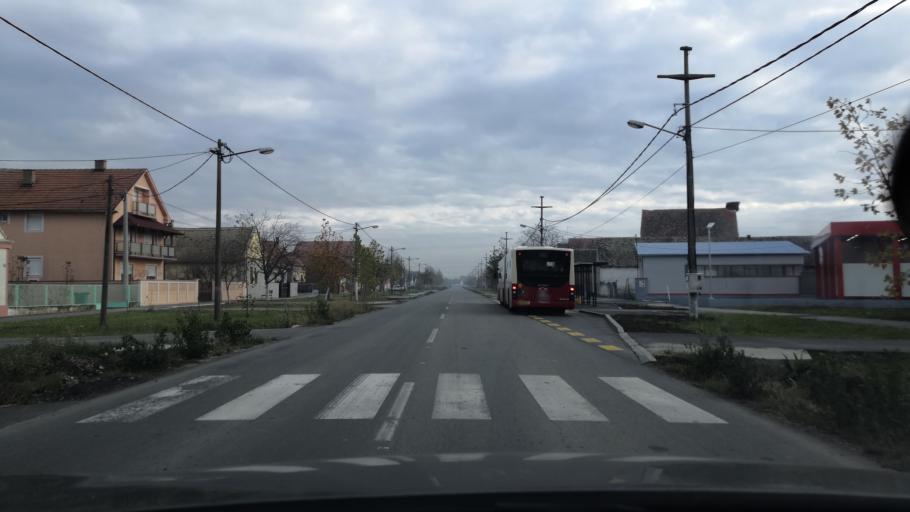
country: RS
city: Ugrinovci
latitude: 44.8793
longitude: 20.1722
